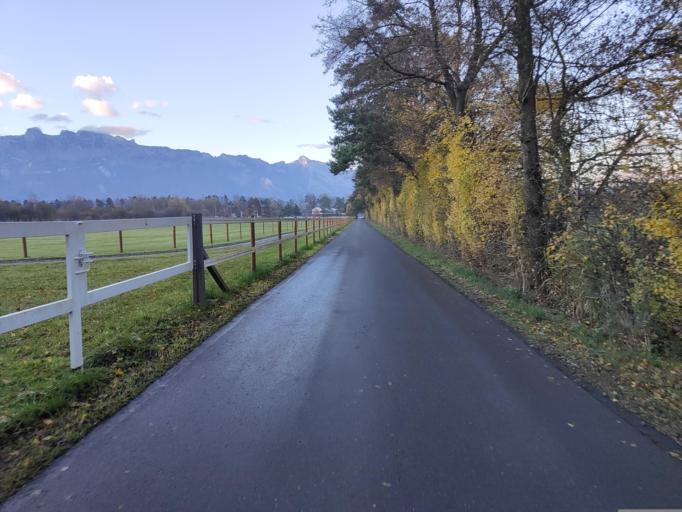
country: LI
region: Planken
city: Planken
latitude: 47.1886
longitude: 9.5252
